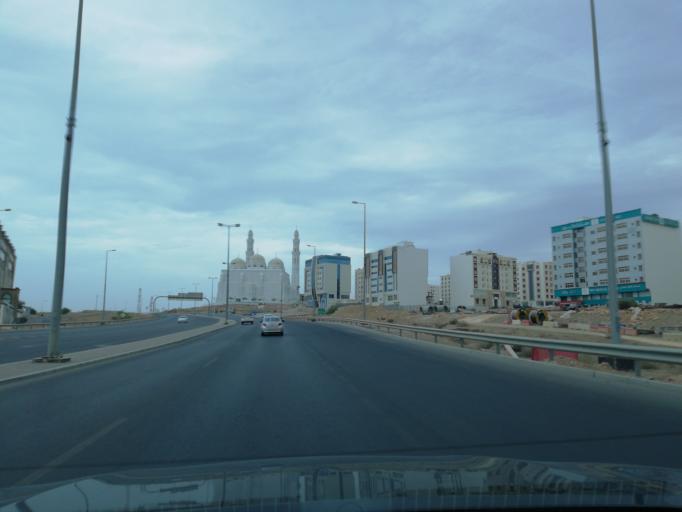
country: OM
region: Muhafazat Masqat
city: Bawshar
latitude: 23.5773
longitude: 58.4095
